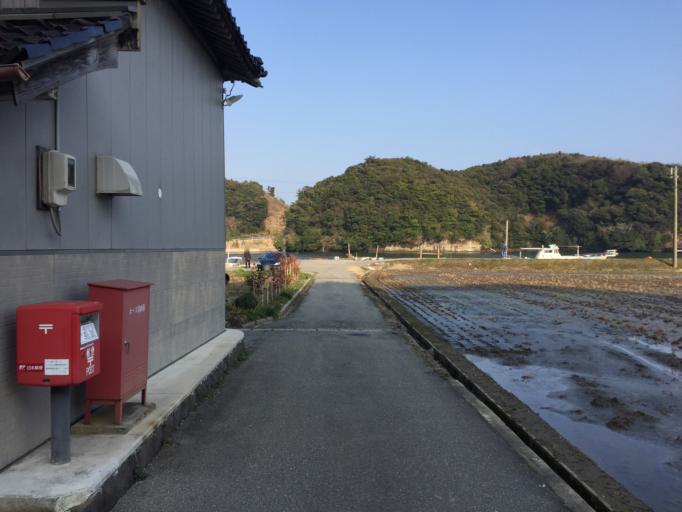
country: JP
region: Ishikawa
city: Nanao
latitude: 37.1133
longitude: 137.0176
